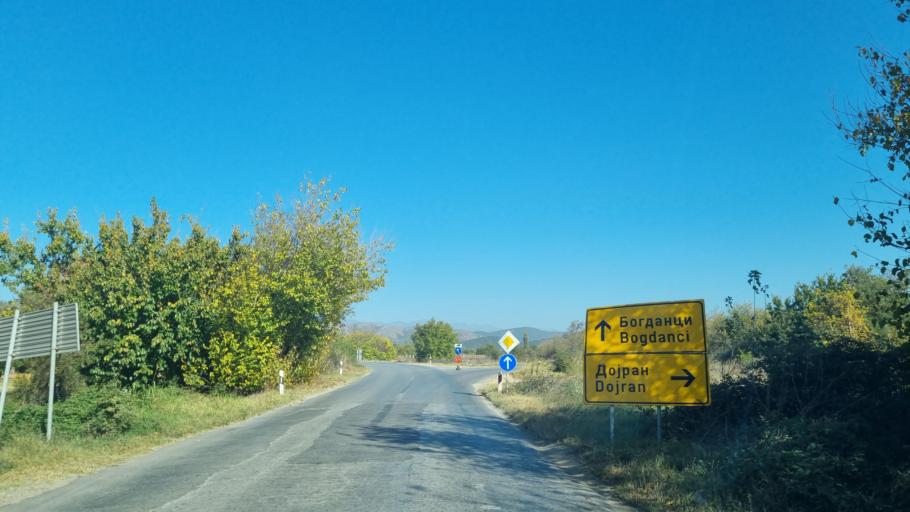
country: MK
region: Bogdanci
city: Bogdanci
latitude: 41.1889
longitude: 22.5589
